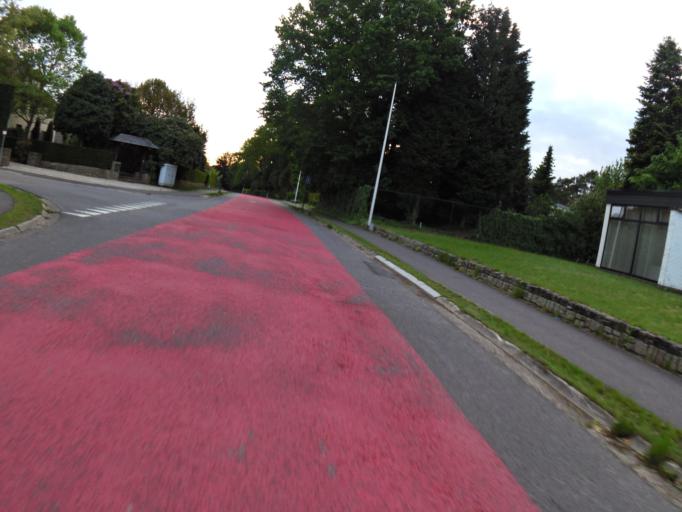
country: BE
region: Flanders
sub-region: Provincie Limburg
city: Genk
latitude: 50.9612
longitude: 5.5085
